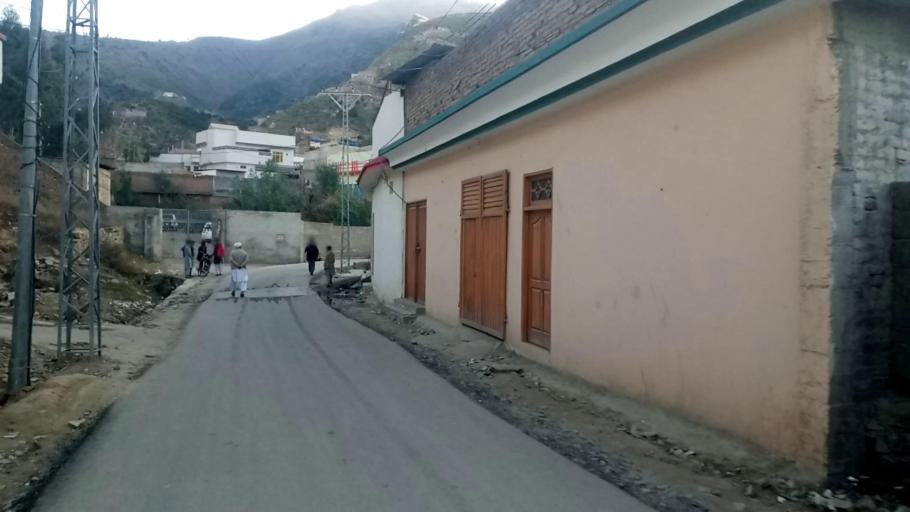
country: PK
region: Khyber Pakhtunkhwa
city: Saidu Sharif
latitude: 34.7397
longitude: 72.3517
